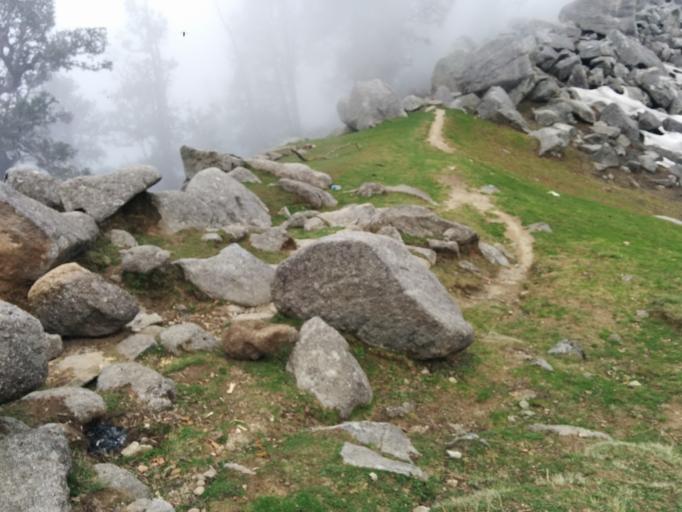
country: IN
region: Himachal Pradesh
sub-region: Kangra
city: Dharmsala
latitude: 32.2804
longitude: 76.3633
